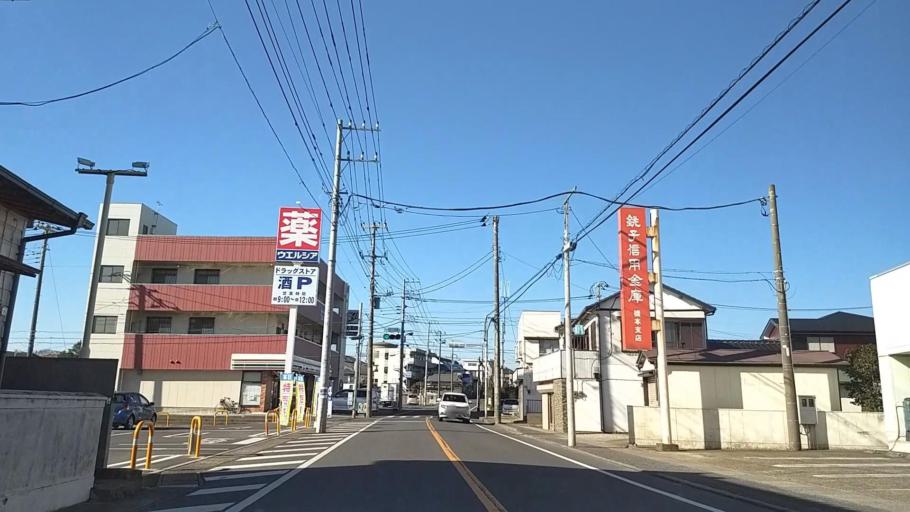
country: JP
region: Chiba
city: Hasaki
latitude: 35.7312
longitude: 140.8578
